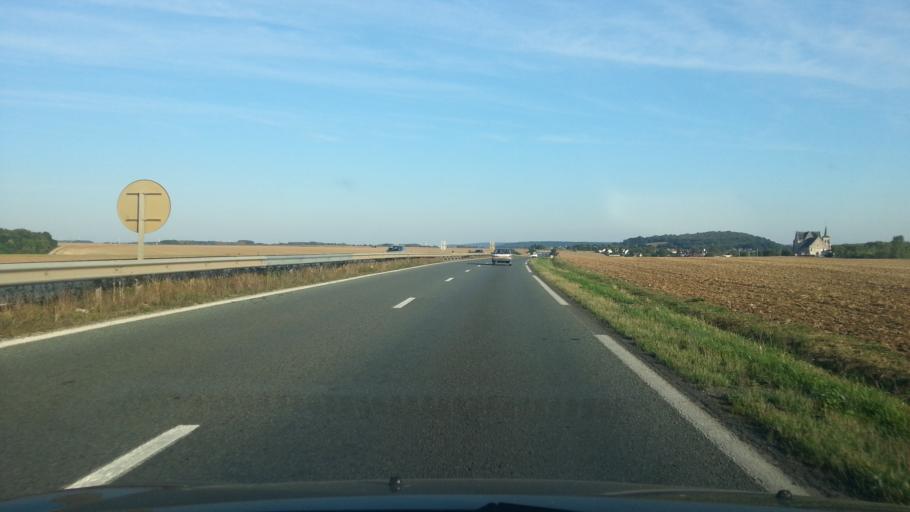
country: FR
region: Picardie
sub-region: Departement de l'Oise
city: Allonne
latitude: 49.4256
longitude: 2.1373
